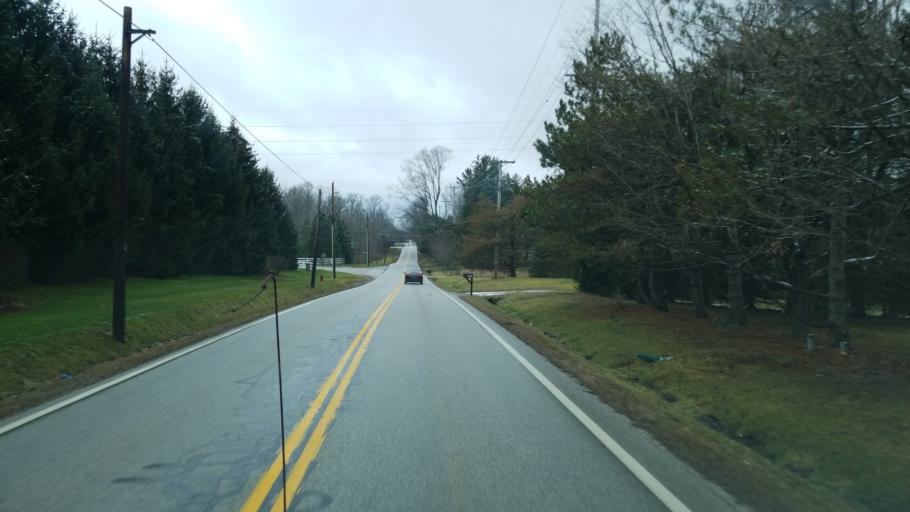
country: US
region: Ohio
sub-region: Summit County
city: Hudson
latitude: 41.2030
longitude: -81.4219
